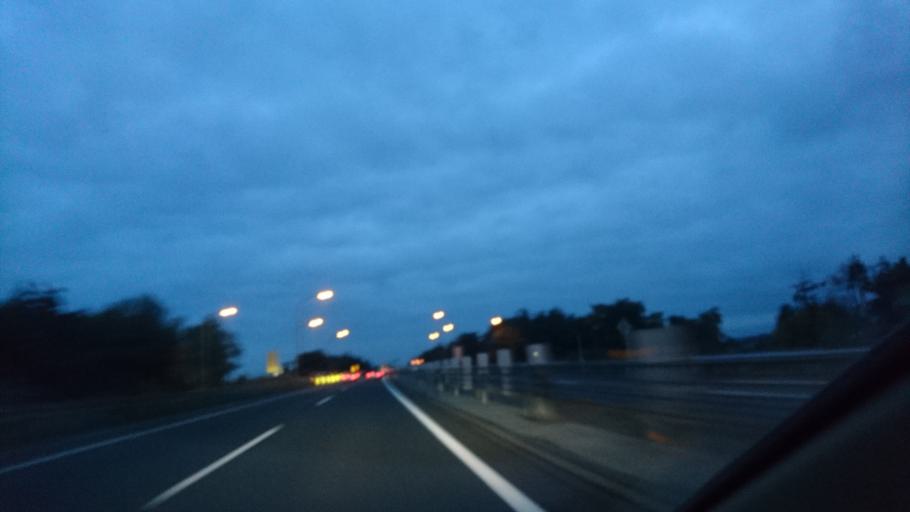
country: JP
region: Iwate
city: Hanamaki
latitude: 39.4443
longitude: 141.1094
